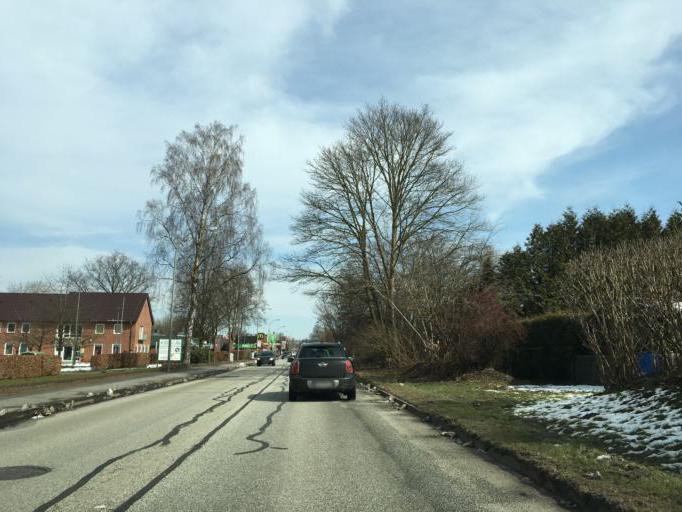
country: DE
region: Schleswig-Holstein
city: Hogersdorf
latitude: 53.9329
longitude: 10.2873
